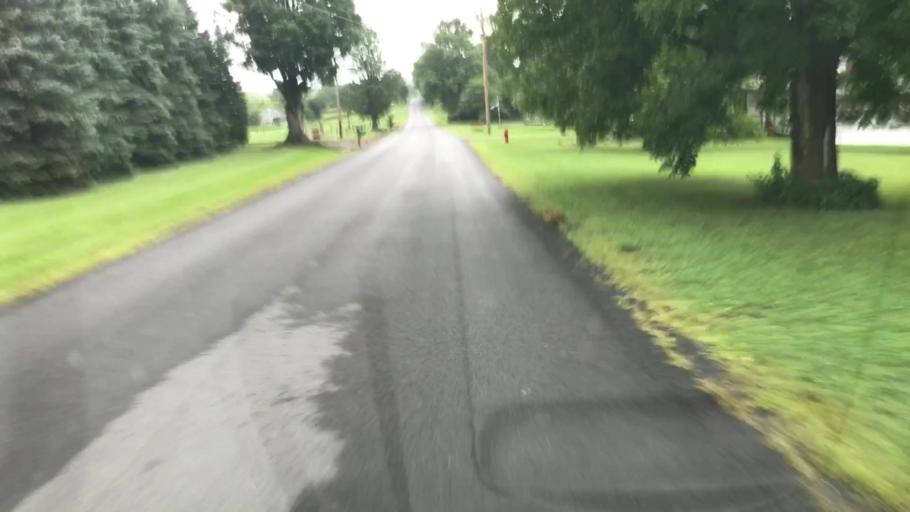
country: US
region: New York
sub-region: Cayuga County
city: Melrose Park
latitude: 42.9345
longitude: -76.5089
